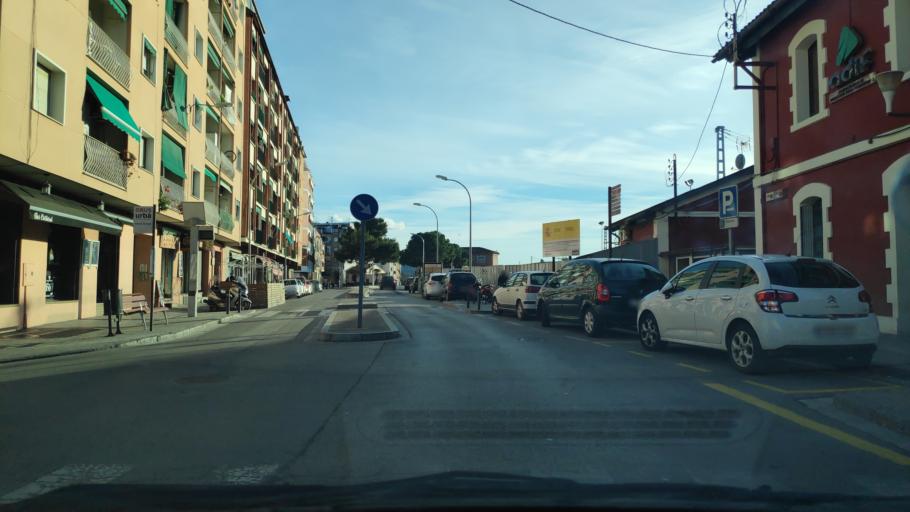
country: ES
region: Catalonia
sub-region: Provincia de Barcelona
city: Mollet del Valles
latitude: 41.5367
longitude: 2.2063
